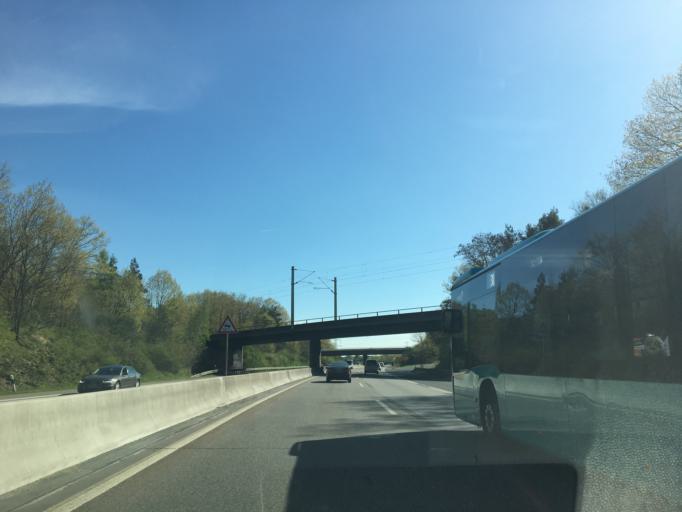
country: DE
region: Hesse
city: Kelsterbach
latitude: 50.0642
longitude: 8.5499
